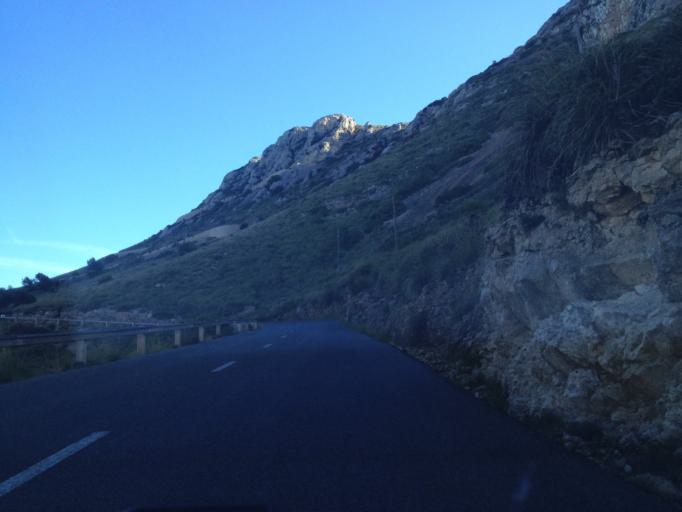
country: ES
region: Balearic Islands
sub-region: Illes Balears
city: Alcudia
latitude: 39.9245
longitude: 3.1077
